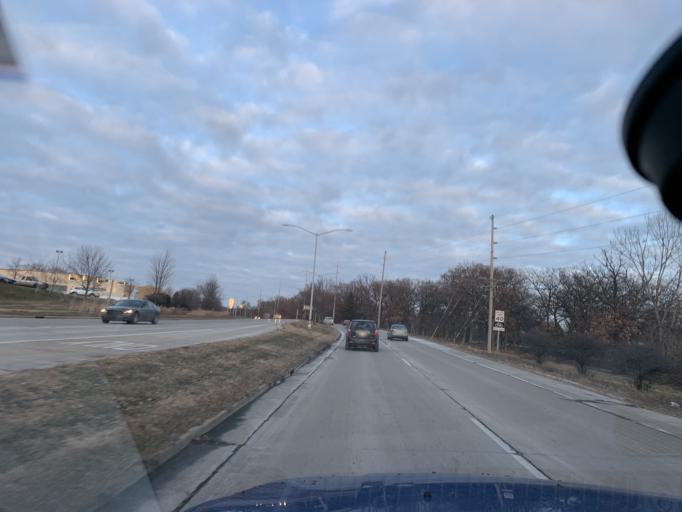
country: US
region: Wisconsin
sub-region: Dane County
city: Madison
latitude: 43.0164
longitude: -89.4228
